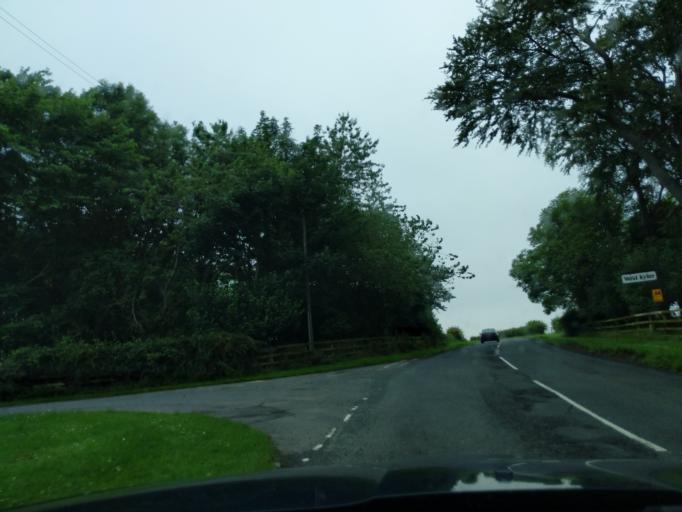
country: GB
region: England
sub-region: Northumberland
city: Lowick
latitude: 55.6572
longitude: -1.9208
